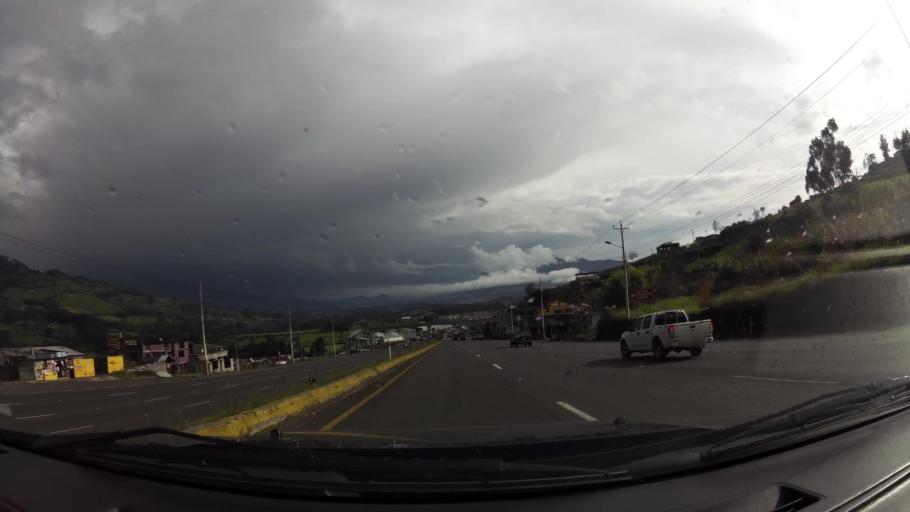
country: EC
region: Pichincha
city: Sangolqui
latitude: -0.3985
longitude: -78.5406
